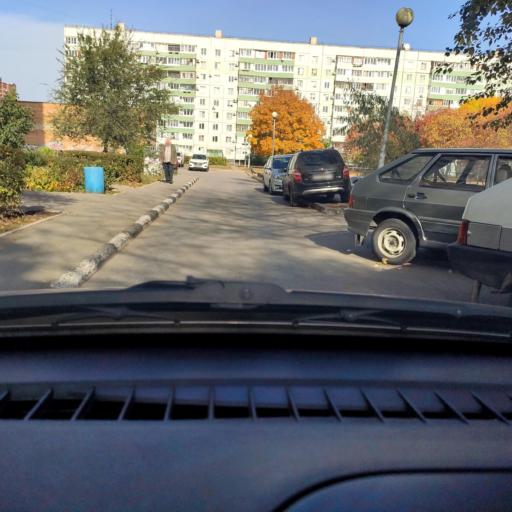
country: RU
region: Samara
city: Tol'yatti
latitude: 53.5414
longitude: 49.3212
